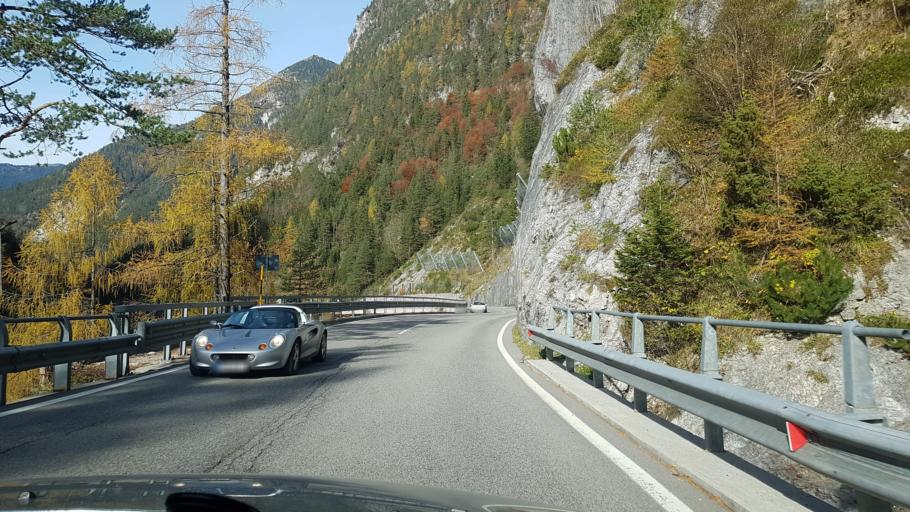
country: IT
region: Veneto
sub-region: Provincia di Belluno
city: Sappada
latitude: 46.5754
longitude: 12.6470
